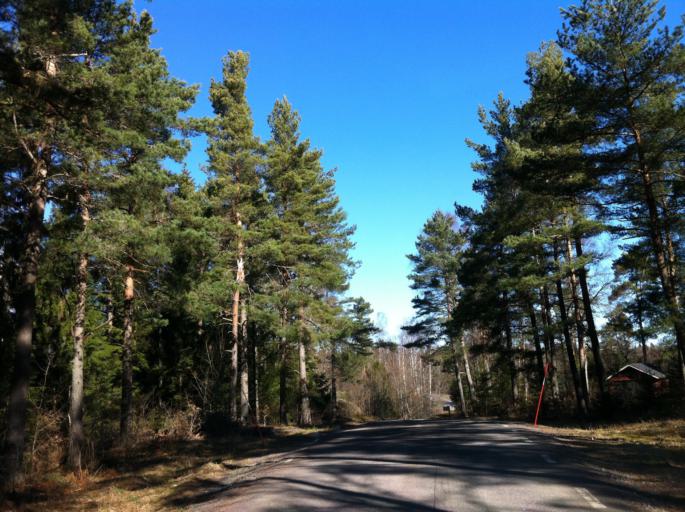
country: SE
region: Vaestra Goetaland
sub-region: Grastorps Kommun
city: Graestorp
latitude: 58.4429
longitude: 12.6109
